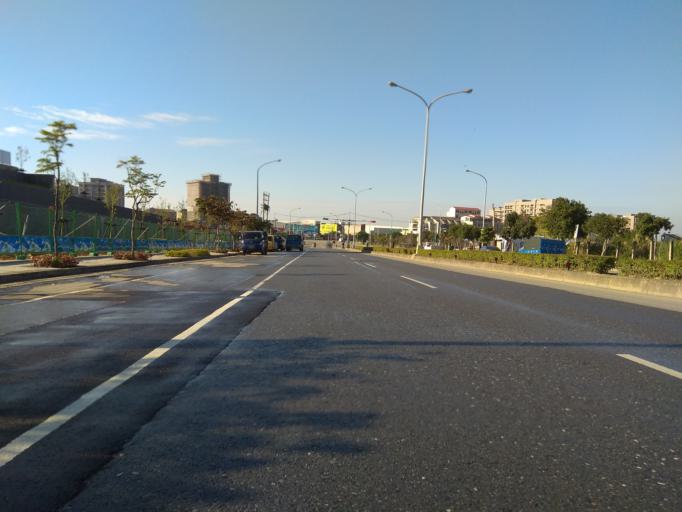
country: TW
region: Taiwan
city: Taoyuan City
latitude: 25.0179
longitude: 121.2172
